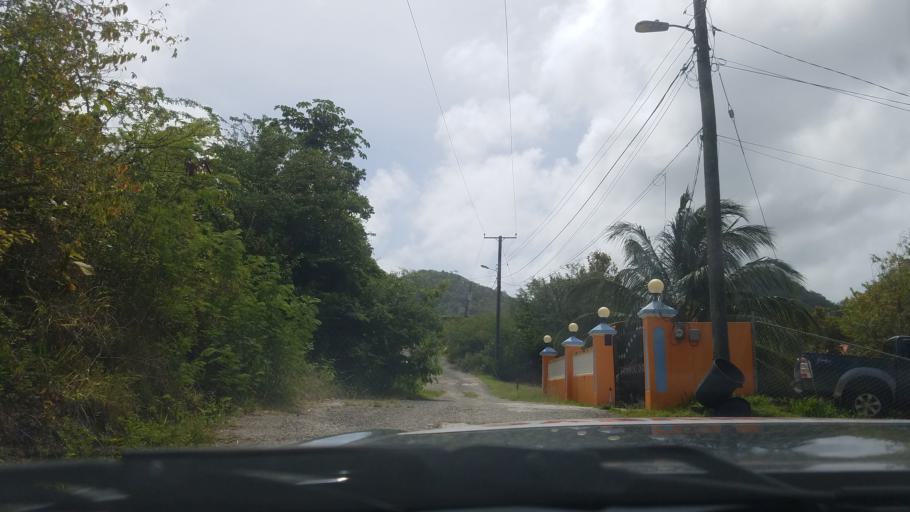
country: LC
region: Gros-Islet
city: Gros Islet
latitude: 14.0468
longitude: -60.9567
